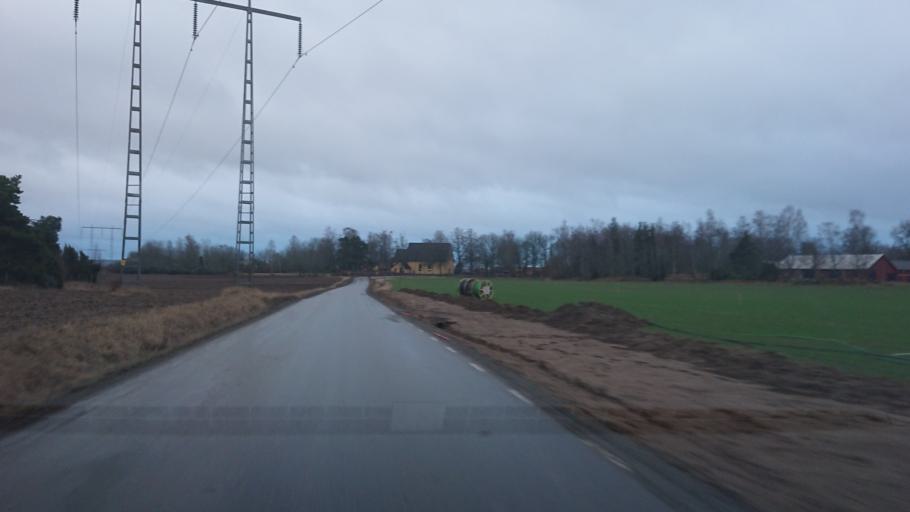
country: SE
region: Uppsala
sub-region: Uppsala Kommun
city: Gamla Uppsala
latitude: 59.9587
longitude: 17.6052
